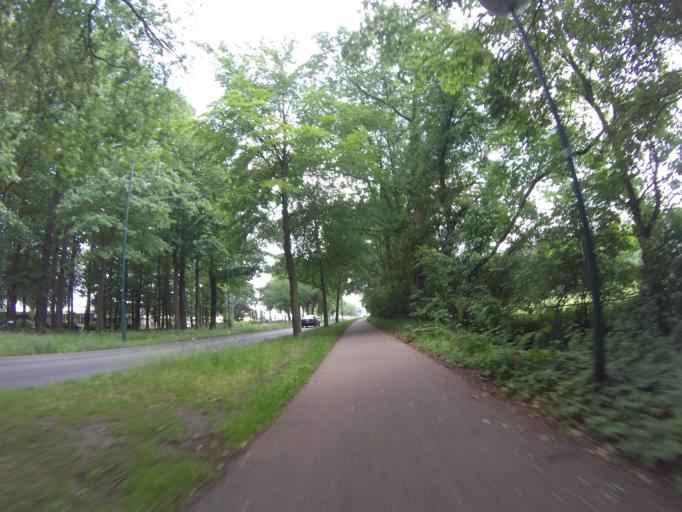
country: NL
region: Utrecht
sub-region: Gemeente Soest
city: Soest
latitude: 52.1826
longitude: 5.2652
